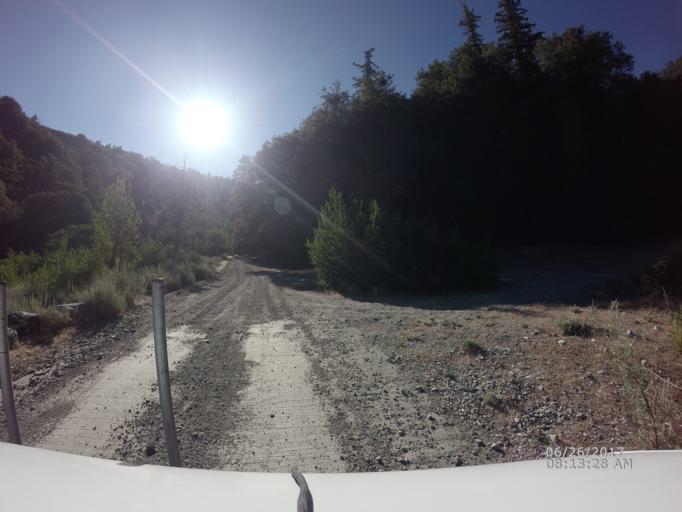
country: US
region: California
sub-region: San Bernardino County
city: Pinon Hills
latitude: 34.3823
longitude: -117.7712
